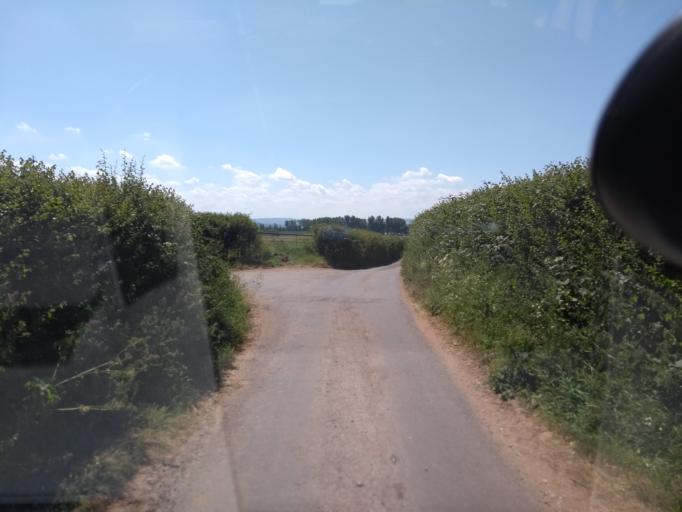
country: GB
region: England
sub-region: Somerset
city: North Petherton
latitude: 51.0667
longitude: -3.0121
